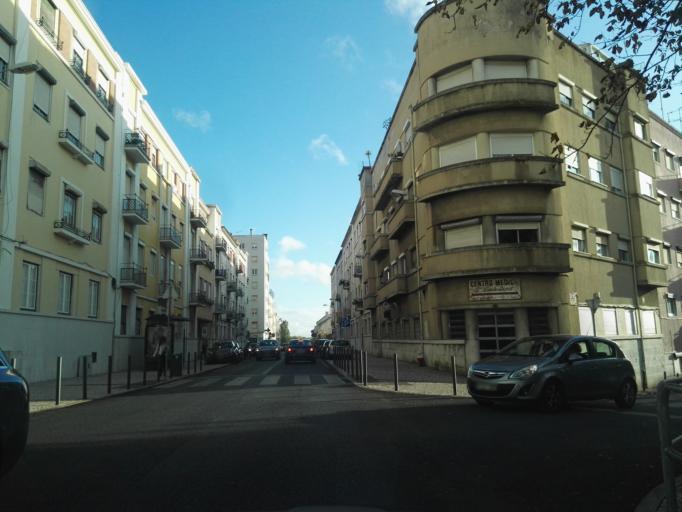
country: PT
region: Lisbon
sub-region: Lisbon
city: Lisbon
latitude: 38.7174
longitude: -9.1696
